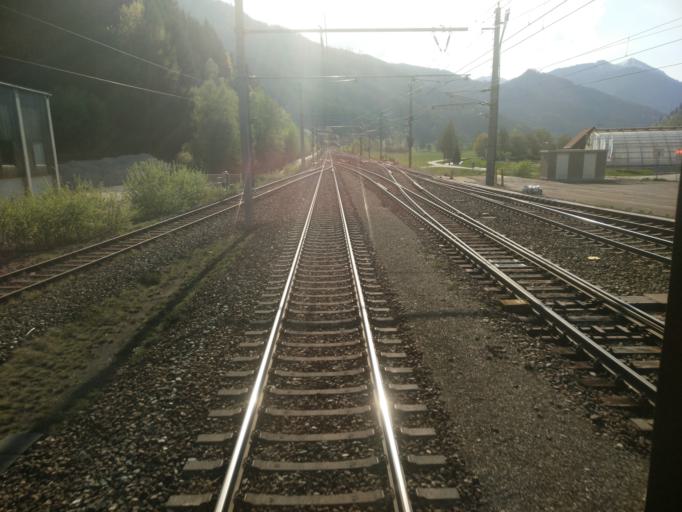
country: AT
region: Styria
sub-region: Politischer Bezirk Leoben
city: Kalwang
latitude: 47.4228
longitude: 14.7412
